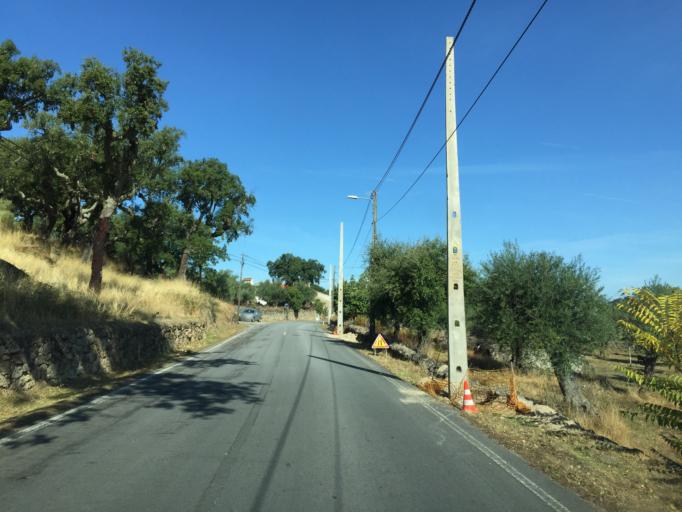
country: PT
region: Portalegre
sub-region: Marvao
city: Marvao
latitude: 39.4207
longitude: -7.3520
